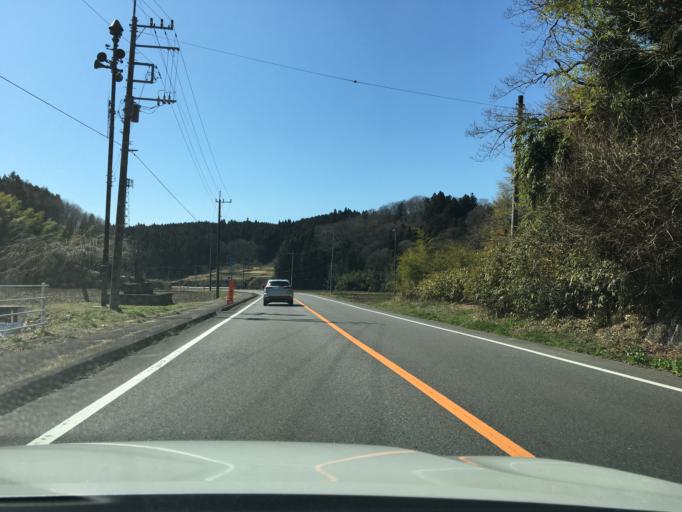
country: JP
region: Tochigi
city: Kuroiso
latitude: 37.0559
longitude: 140.1739
